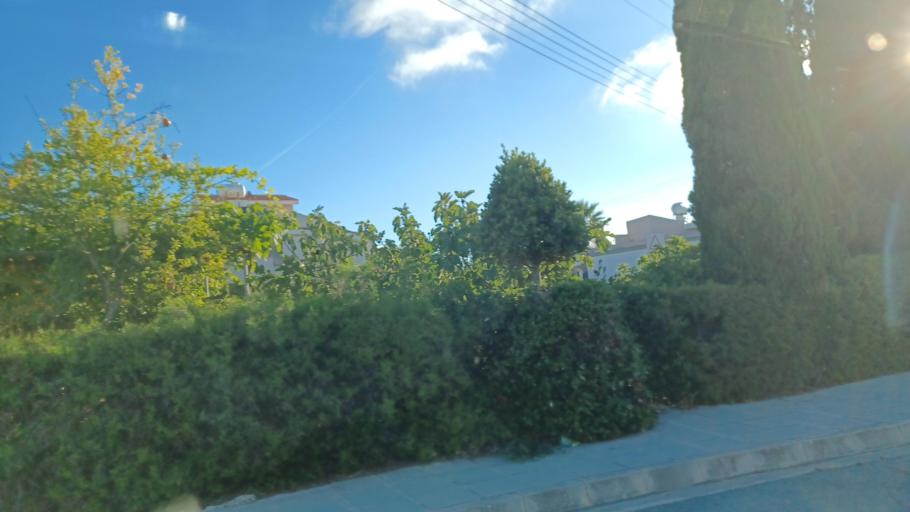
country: CY
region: Pafos
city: Tala
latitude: 34.8544
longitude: 32.4570
